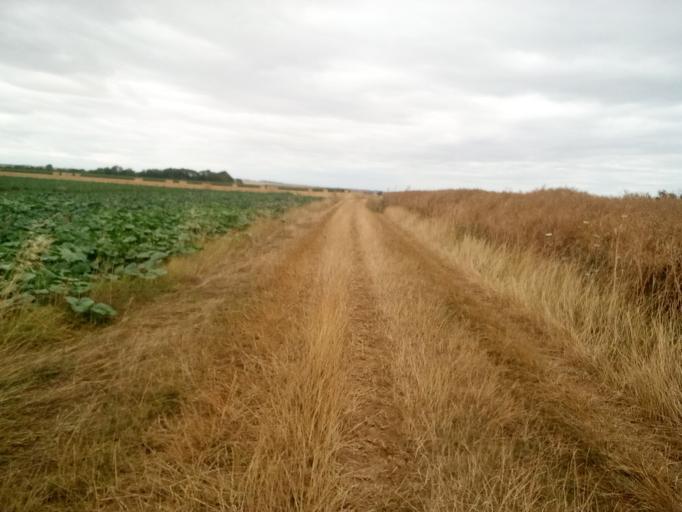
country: FR
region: Lower Normandy
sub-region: Departement du Calvados
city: Clinchamps-sur-Orne
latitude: 49.0591
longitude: -0.4125
